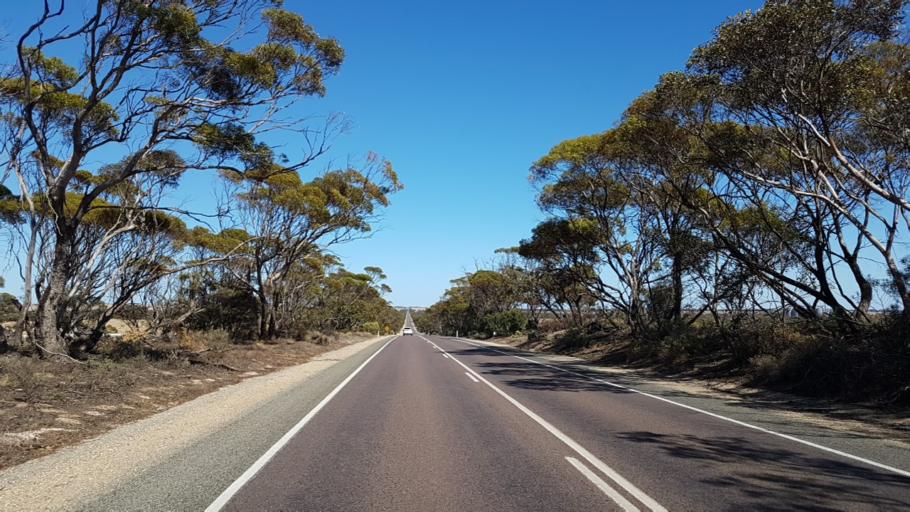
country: AU
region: South Australia
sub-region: Copper Coast
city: Kadina
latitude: -34.0531
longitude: 137.9958
